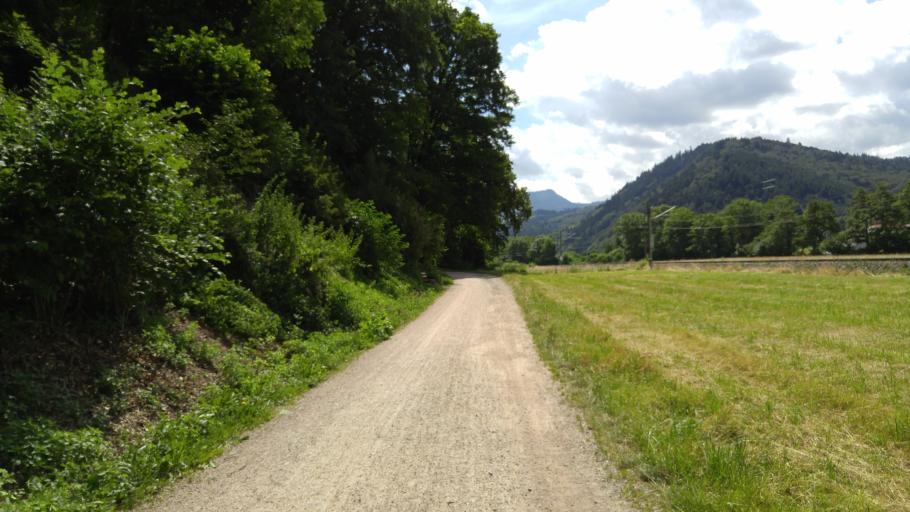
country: DE
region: Baden-Wuerttemberg
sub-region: Freiburg Region
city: Muenstertal/Schwarzwald
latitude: 47.8689
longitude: 7.7454
